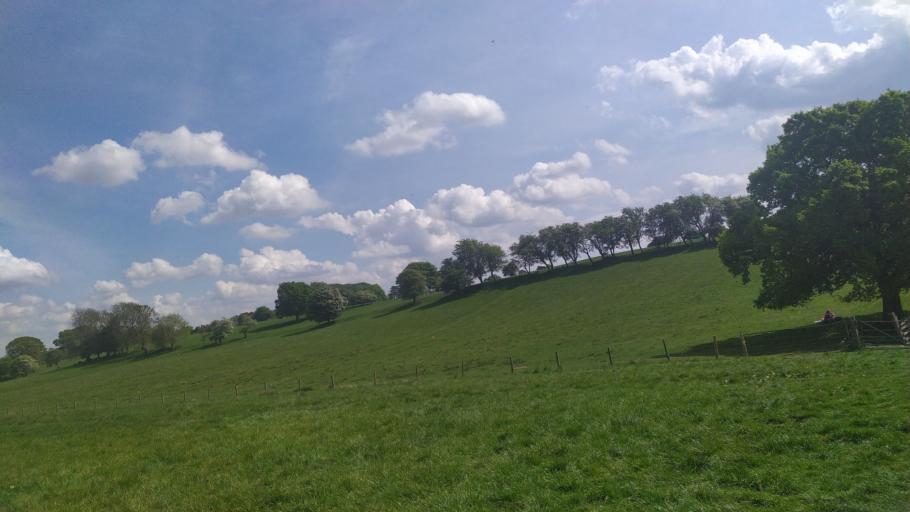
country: GB
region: England
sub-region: City and Borough of Leeds
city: Chapel Allerton
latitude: 53.8667
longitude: -1.5603
